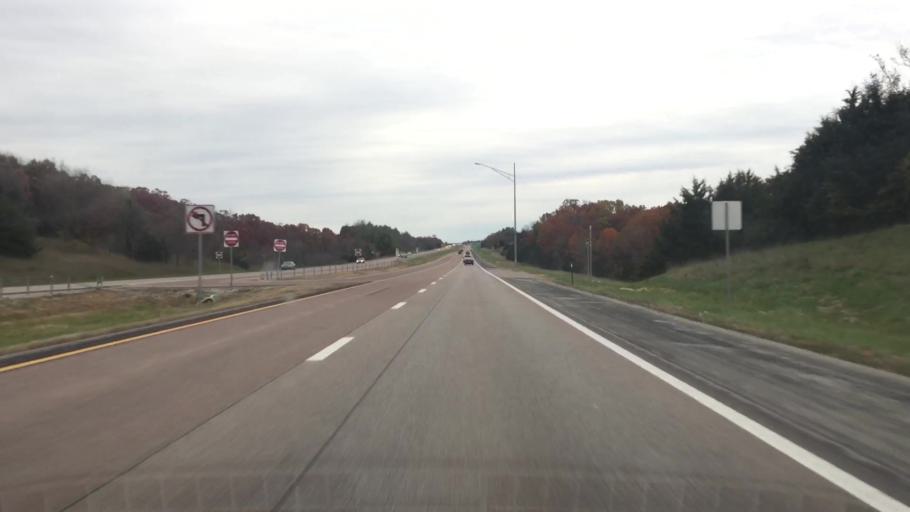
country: US
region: Missouri
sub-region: Boone County
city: Ashland
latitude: 38.7493
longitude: -92.2532
